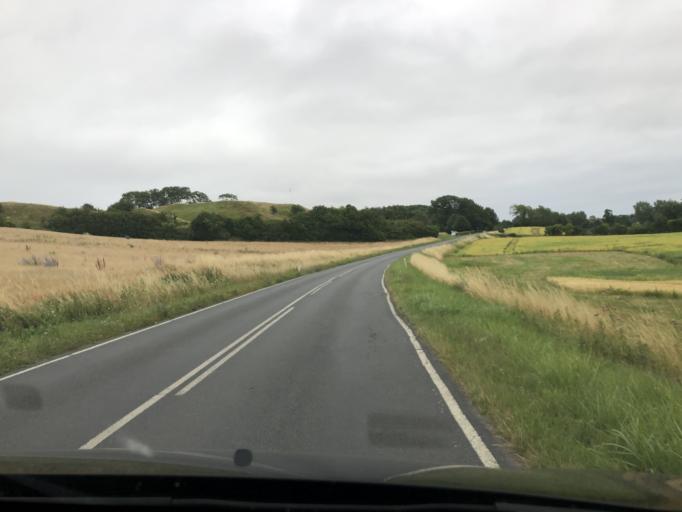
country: DK
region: South Denmark
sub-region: AEro Kommune
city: AEroskobing
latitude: 54.9217
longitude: 10.2786
